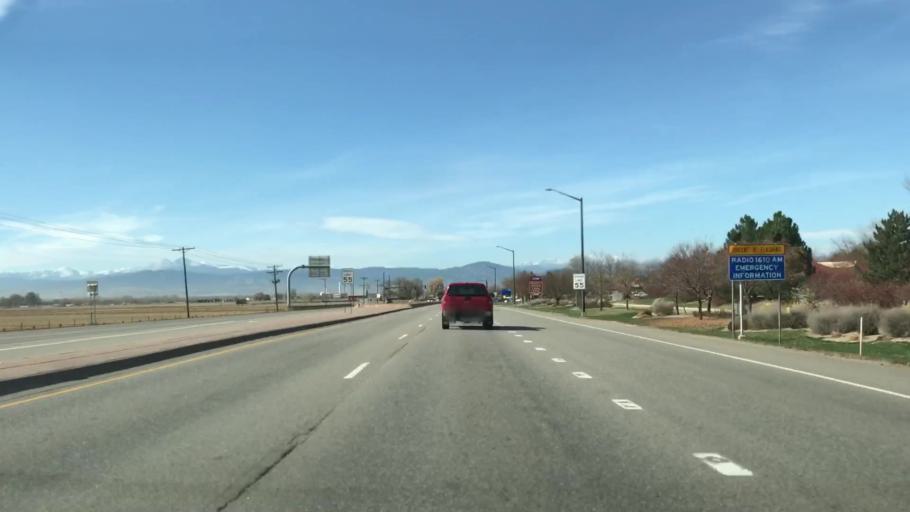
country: US
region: Colorado
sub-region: Larimer County
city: Loveland
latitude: 40.4070
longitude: -104.9984
